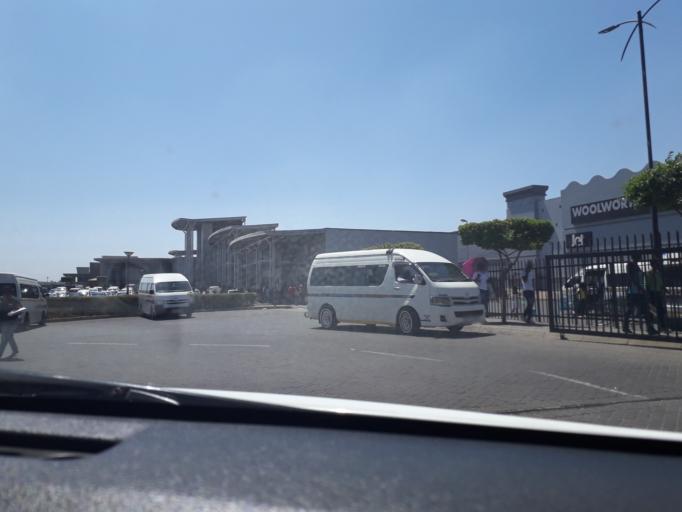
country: ZA
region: Gauteng
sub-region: City of Johannesburg Metropolitan Municipality
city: Modderfontein
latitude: -26.1079
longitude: 28.2237
